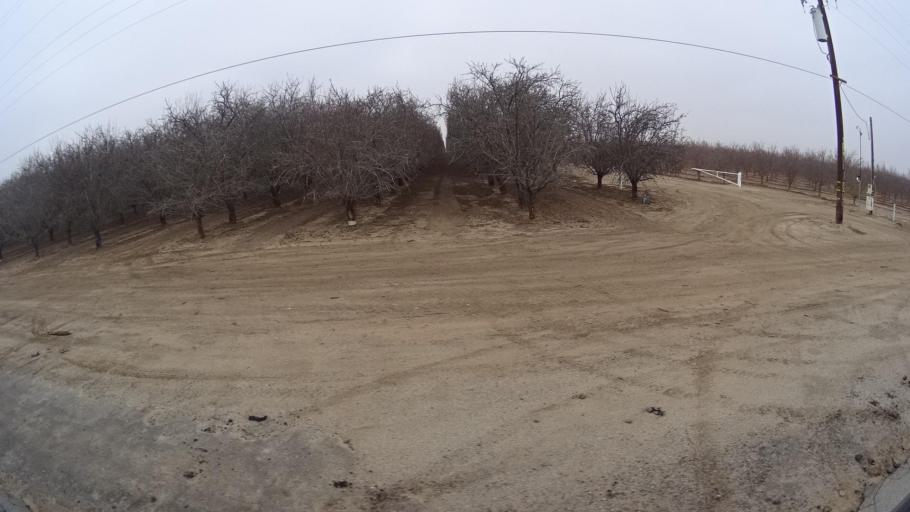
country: US
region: California
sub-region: Kern County
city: Maricopa
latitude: 35.0938
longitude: -119.2876
